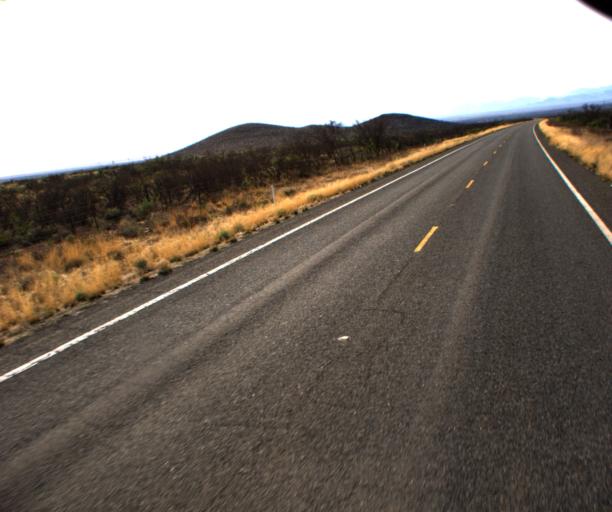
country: US
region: Arizona
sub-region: Cochise County
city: Willcox
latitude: 32.1843
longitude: -109.6705
